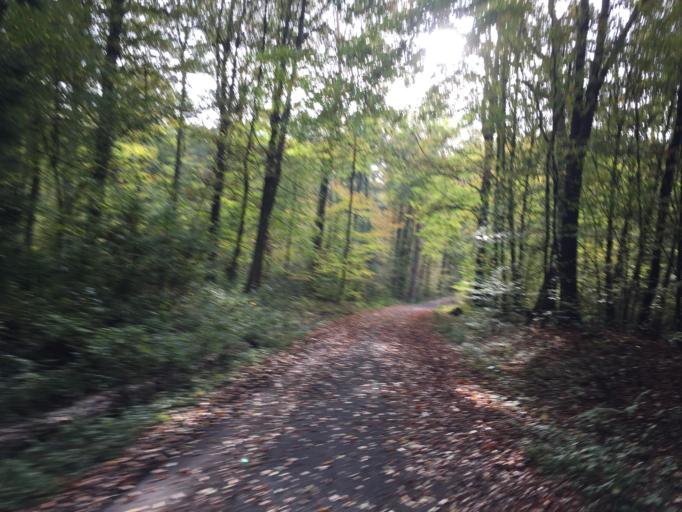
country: DE
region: Hesse
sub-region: Regierungsbezirk Giessen
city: Grunberg
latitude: 50.5852
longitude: 8.9886
